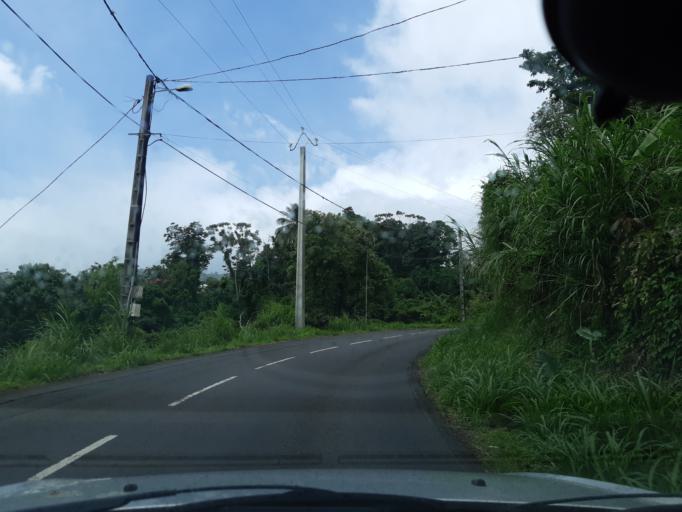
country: GP
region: Guadeloupe
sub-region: Guadeloupe
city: Saint-Claude
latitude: 16.0113
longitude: -61.6921
